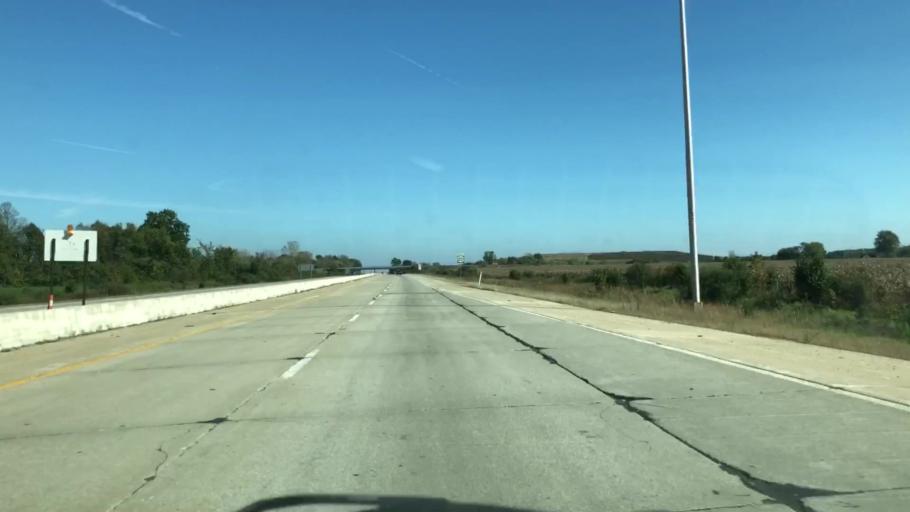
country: US
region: Indiana
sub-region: Elkhart County
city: Elkhart
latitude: 41.6338
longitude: -85.9917
